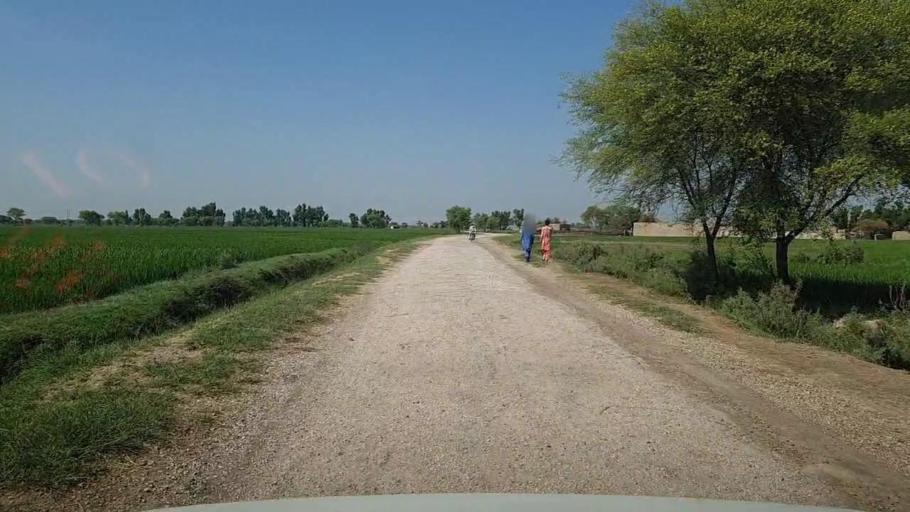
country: PK
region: Sindh
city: Kandhkot
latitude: 28.3279
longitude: 69.3670
